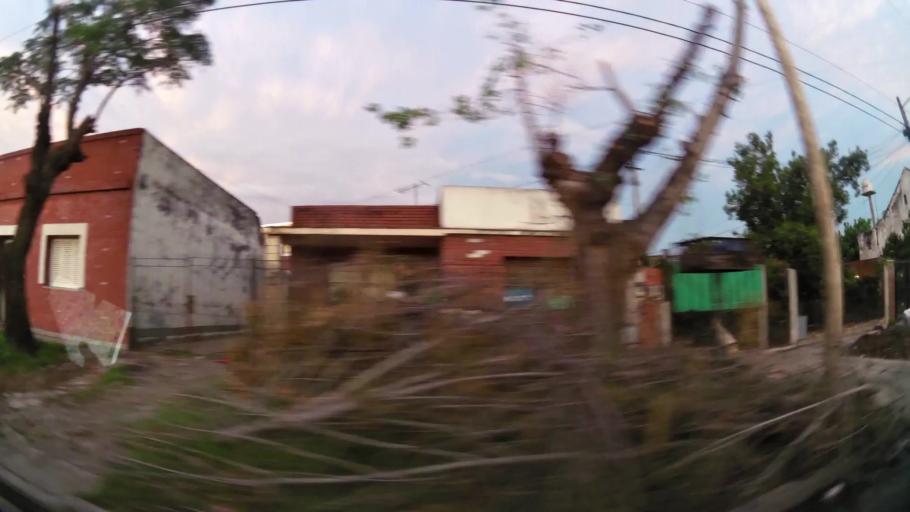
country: AR
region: Buenos Aires
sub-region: Partido de Lomas de Zamora
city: Lomas de Zamora
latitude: -34.7519
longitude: -58.3619
